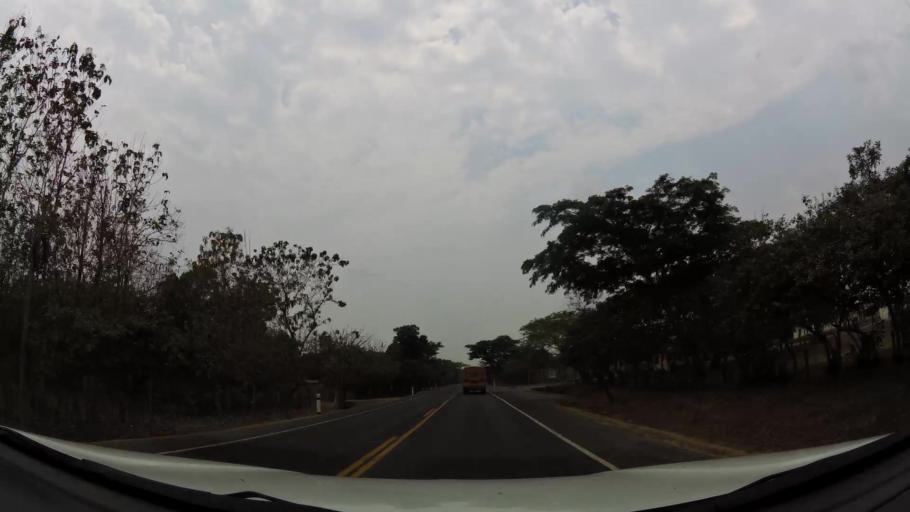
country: NI
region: Chinandega
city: Chichigalpa
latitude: 12.5968
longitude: -87.0351
